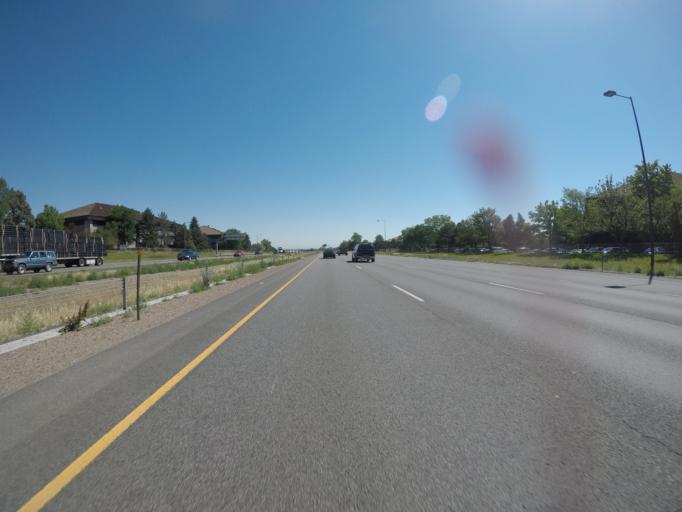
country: US
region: Colorado
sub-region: Jefferson County
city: Applewood
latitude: 39.7428
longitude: -105.1555
